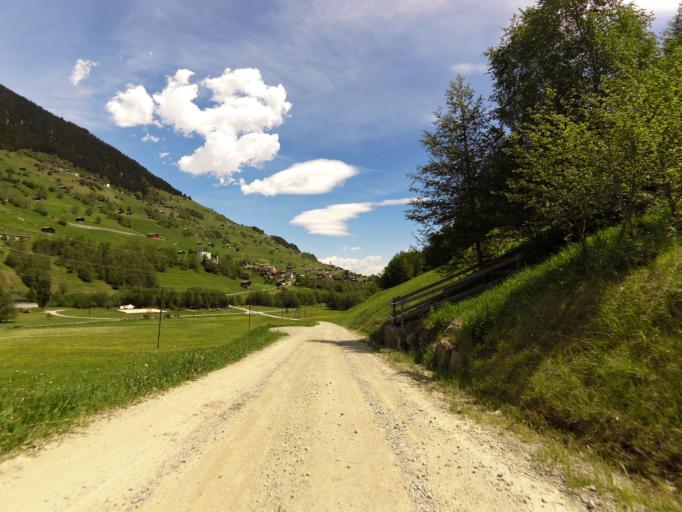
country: CH
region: Grisons
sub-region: Surselva District
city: Disentis
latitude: 46.7193
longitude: 8.9119
